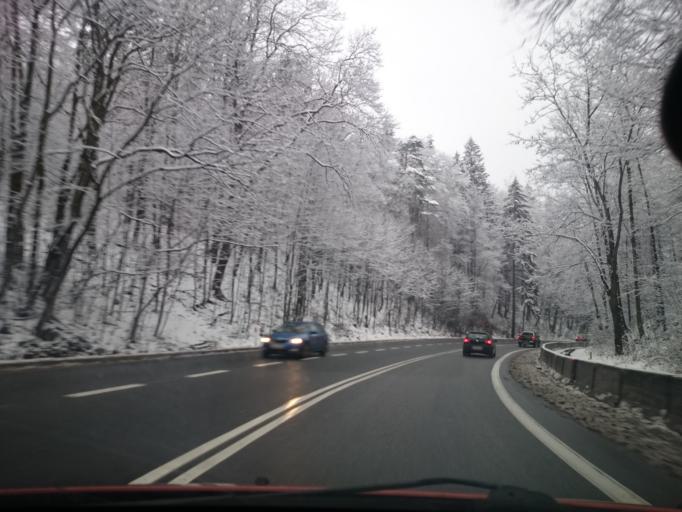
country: PL
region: Lower Silesian Voivodeship
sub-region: Powiat zabkowicki
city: Bardo
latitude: 50.4820
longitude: 16.7106
